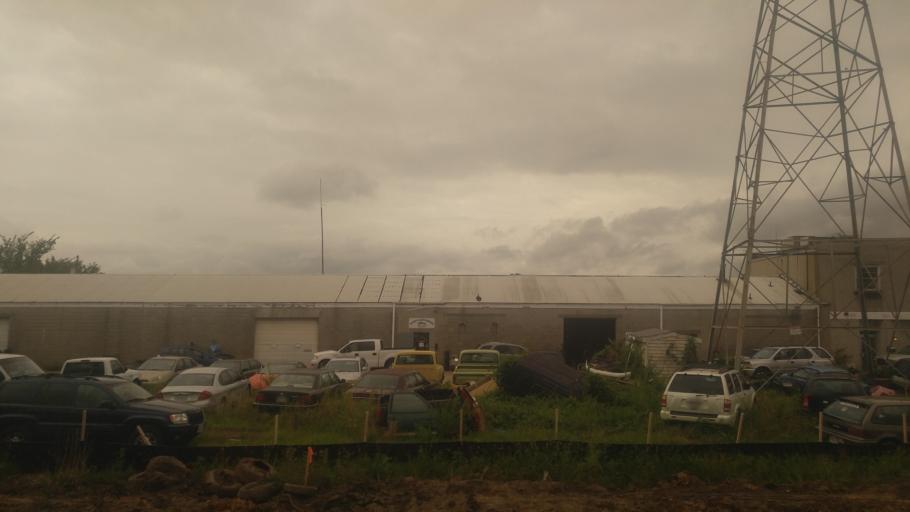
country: US
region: Virginia
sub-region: Henrico County
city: Dumbarton
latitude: 37.6128
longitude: -77.4940
